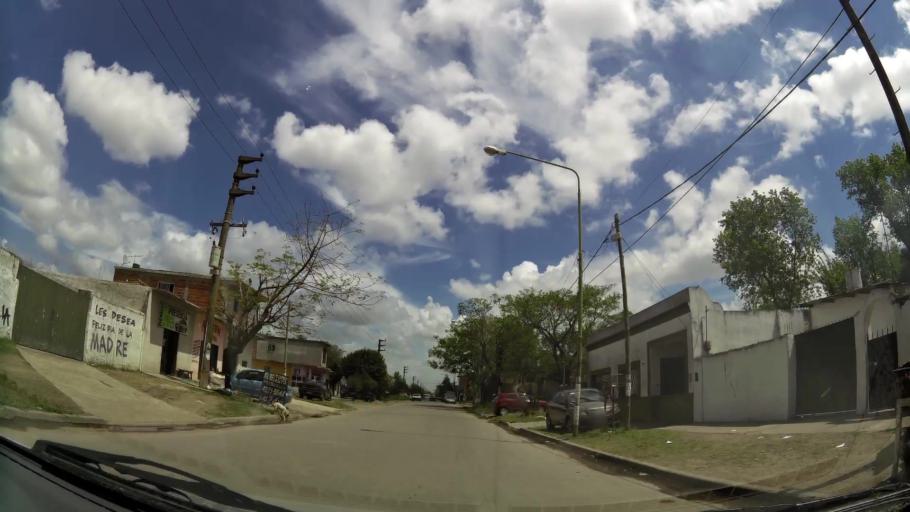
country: AR
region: Buenos Aires
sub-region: Partido de Quilmes
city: Quilmes
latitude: -34.8132
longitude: -58.2325
